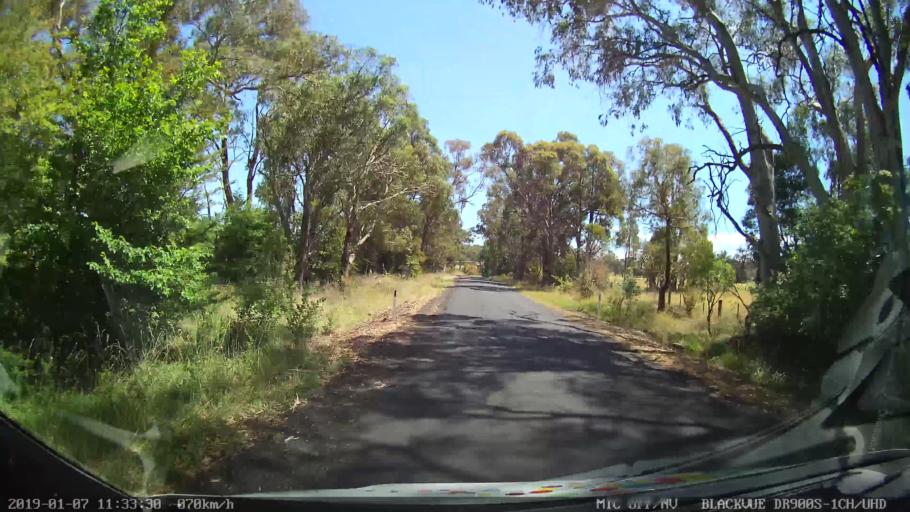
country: AU
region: New South Wales
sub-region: Armidale Dumaresq
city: Armidale
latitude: -30.3992
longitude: 151.5610
